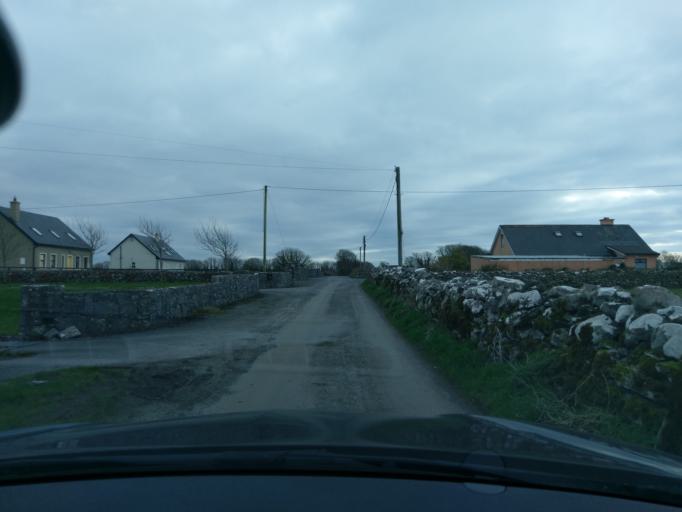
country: IE
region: Connaught
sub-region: County Galway
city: Oranmore
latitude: 53.2013
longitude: -8.9224
